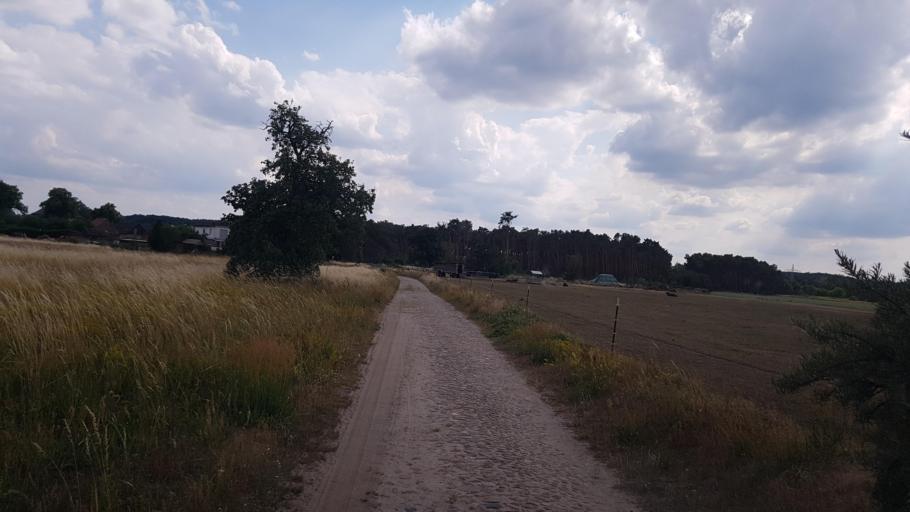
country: DE
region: Brandenburg
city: Golzow
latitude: 52.2488
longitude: 12.5795
